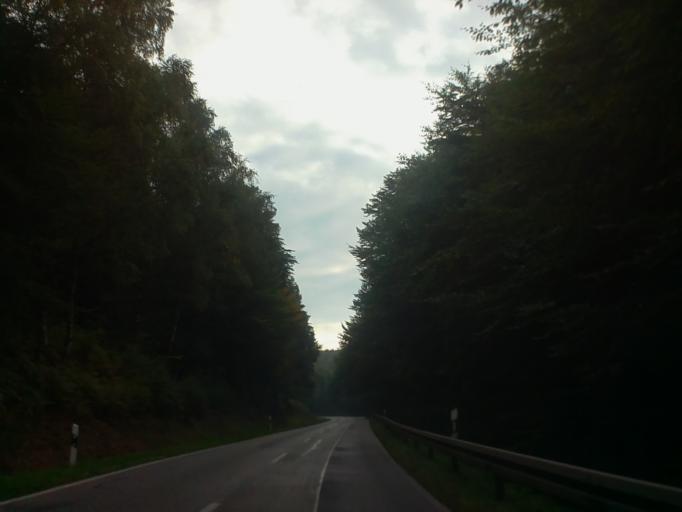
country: DE
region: Hesse
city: Hochst im Odenwald
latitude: 49.7833
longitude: 8.9786
